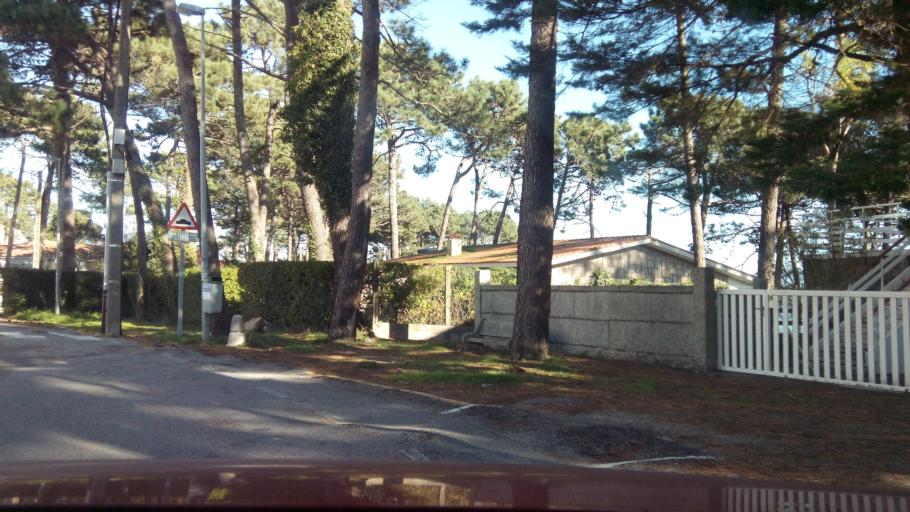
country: ES
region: Galicia
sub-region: Provincia de Pontevedra
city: O Grove
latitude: 42.4547
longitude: -8.9250
